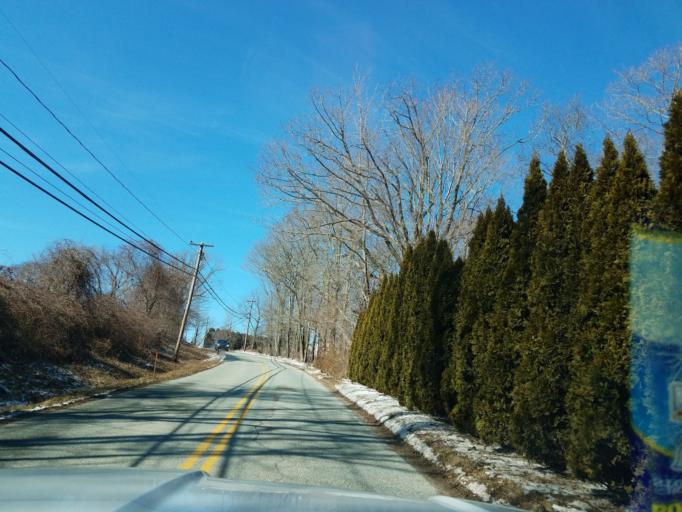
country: US
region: Connecticut
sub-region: New London County
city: Old Mystic
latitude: 41.4512
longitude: -71.9166
